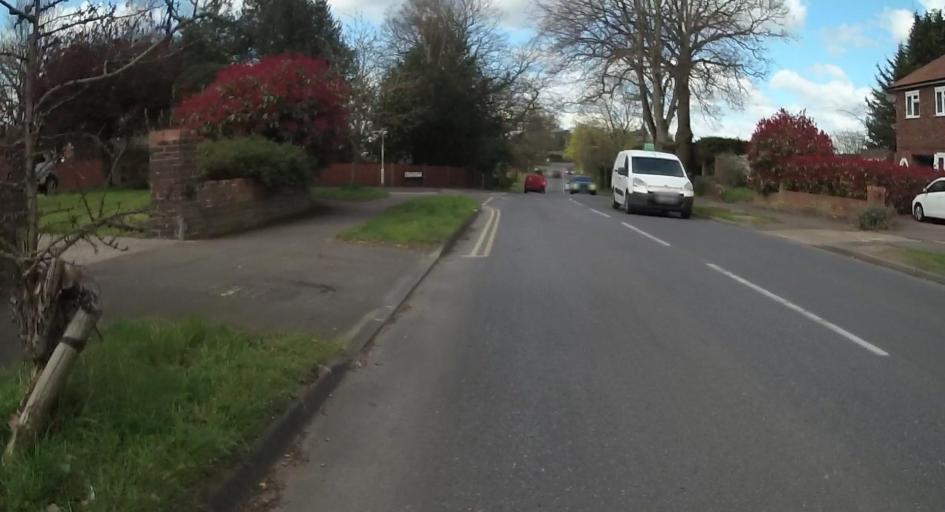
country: GB
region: England
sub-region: Surrey
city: West Byfleet
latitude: 51.3494
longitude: -0.5106
